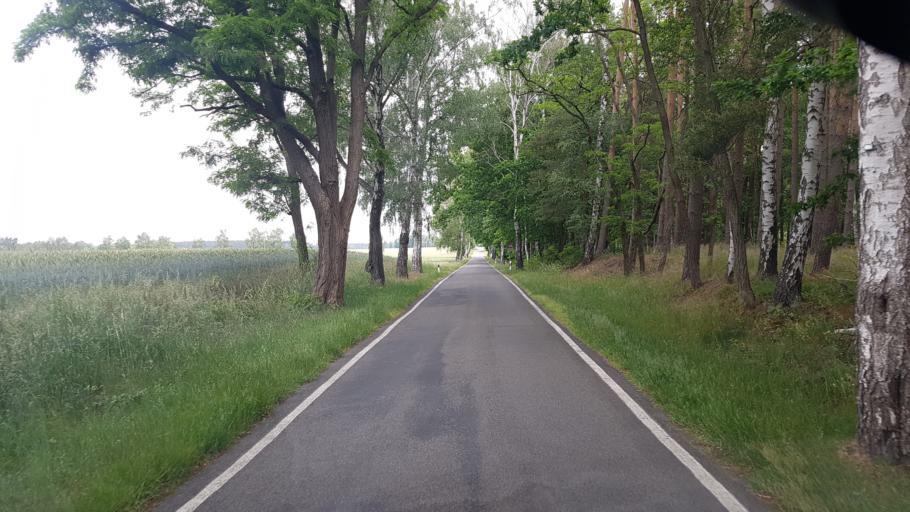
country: DE
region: Brandenburg
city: Lebusa
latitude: 51.8011
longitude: 13.4539
